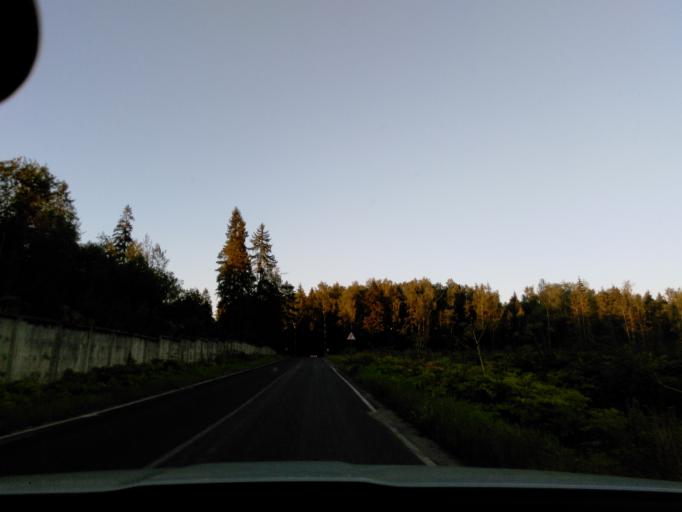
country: RU
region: Moskovskaya
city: Solnechnogorsk
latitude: 56.1309
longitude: 36.8768
